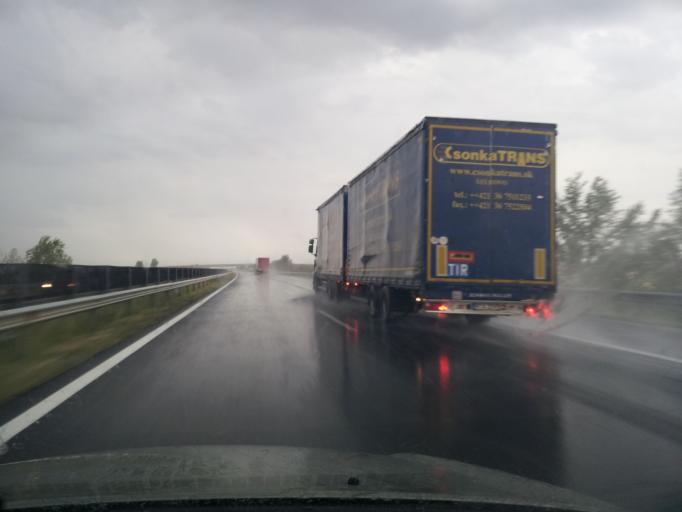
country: HU
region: Borsod-Abauj-Zemplen
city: Malyi
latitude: 48.0316
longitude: 20.8612
